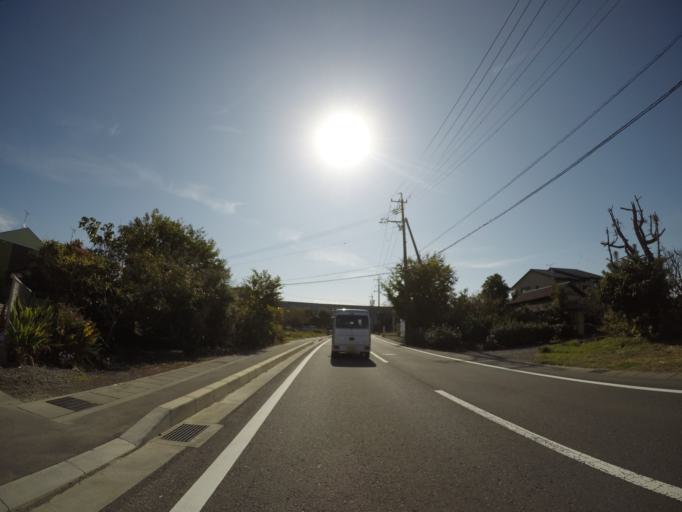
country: JP
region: Shizuoka
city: Shizuoka-shi
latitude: 34.9649
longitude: 138.4247
